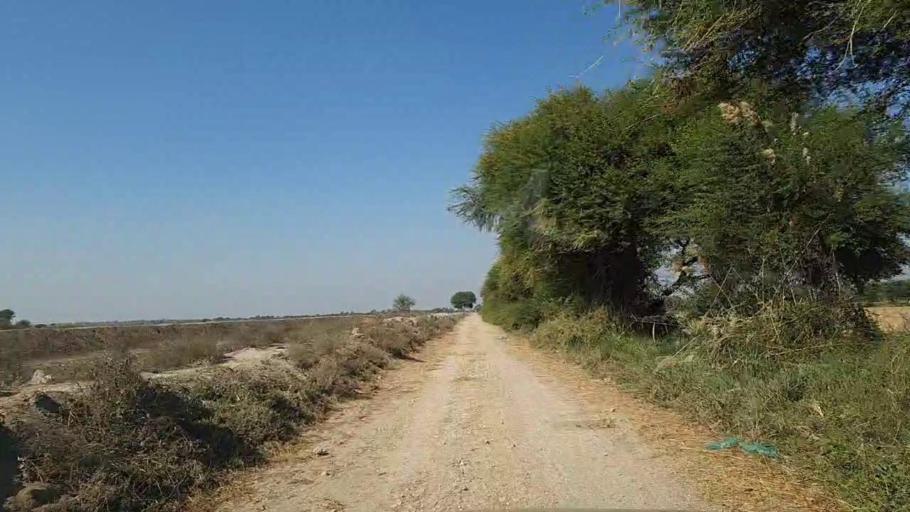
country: PK
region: Sindh
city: Mirpur Batoro
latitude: 24.7199
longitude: 68.2350
